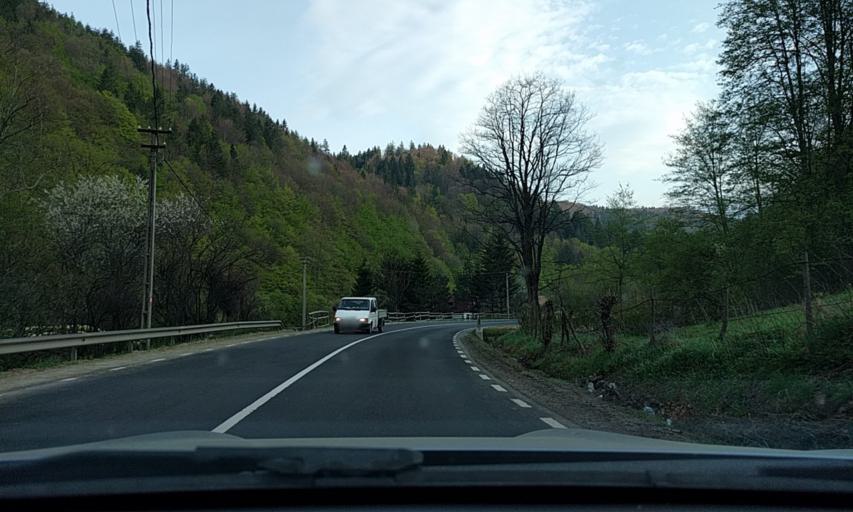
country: RO
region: Covasna
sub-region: Comuna Bretcu
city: Bretcu
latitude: 46.0757
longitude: 26.3950
